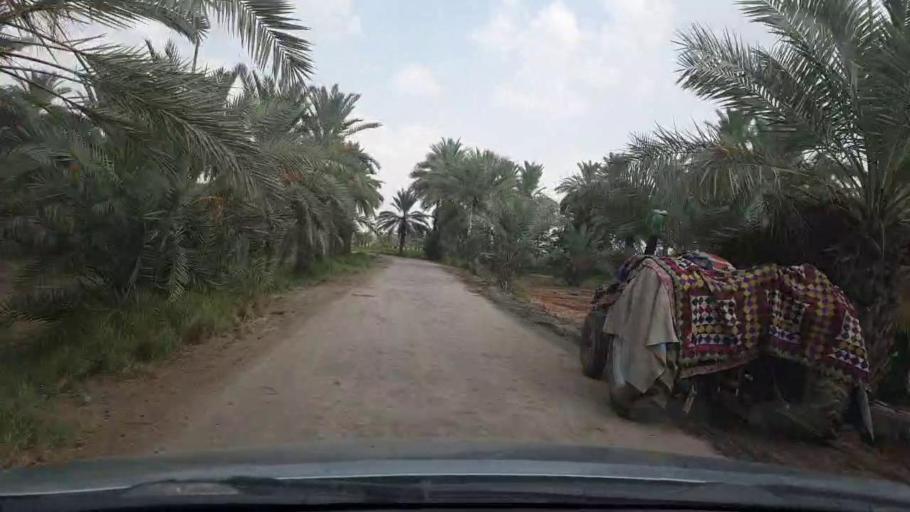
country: PK
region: Sindh
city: Khairpur
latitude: 27.4654
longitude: 68.7571
